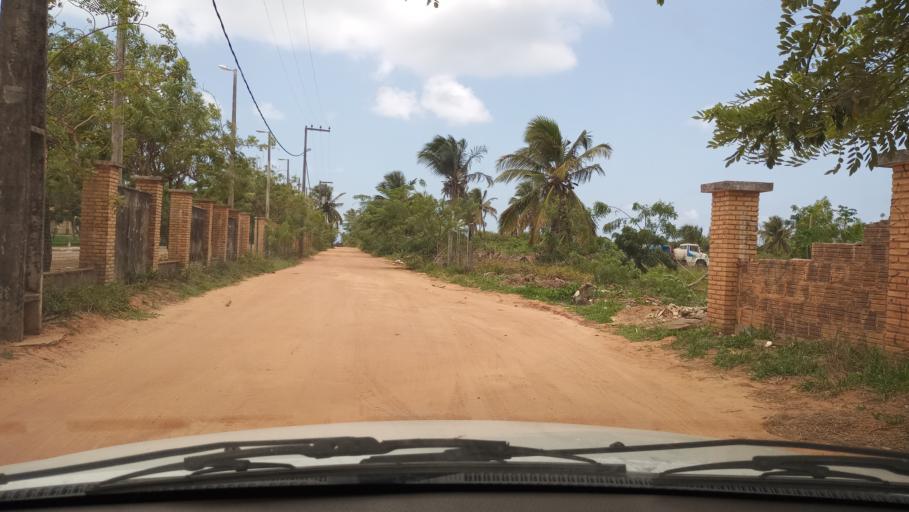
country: BR
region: Rio Grande do Norte
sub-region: Ares
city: Ares
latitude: -6.2380
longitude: -35.0401
